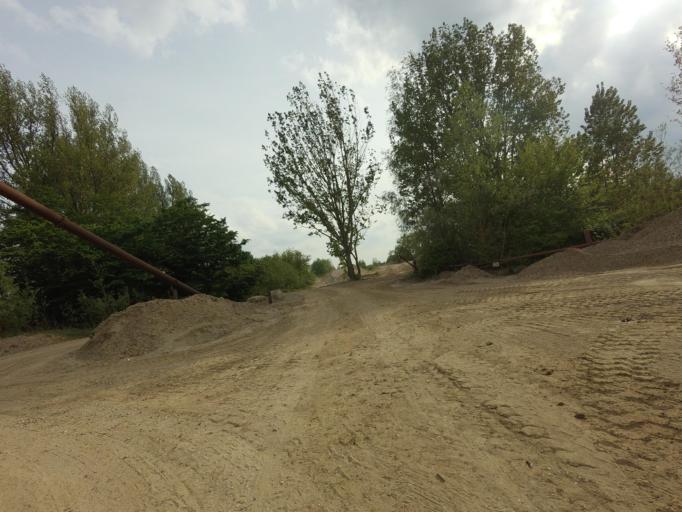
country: DE
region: Lower Saxony
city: Nordstemmen
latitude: 52.1653
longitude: 9.7566
